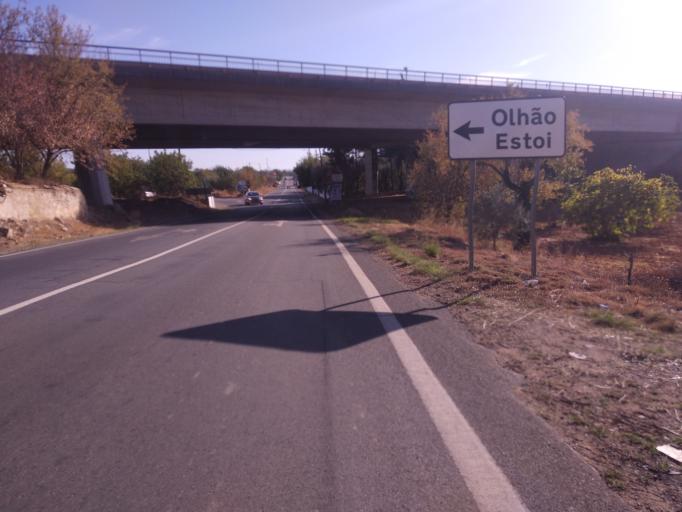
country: PT
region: Faro
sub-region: Sao Bras de Alportel
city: Sao Bras de Alportel
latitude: 37.1000
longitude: -7.9051
